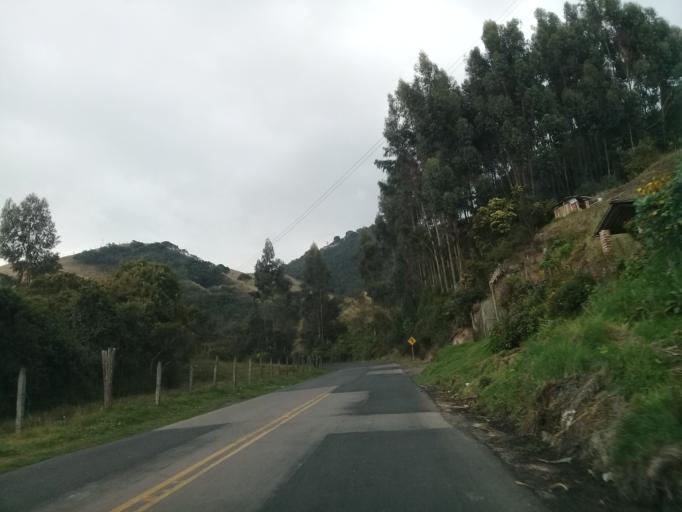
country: CO
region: Cundinamarca
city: Zipaquira
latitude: 5.0437
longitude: -74.0482
